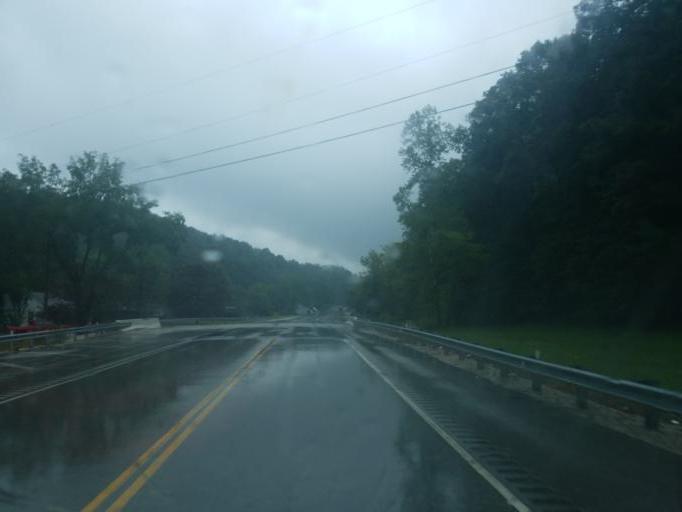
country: US
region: Kentucky
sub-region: Rowan County
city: Morehead
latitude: 38.2476
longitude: -83.3430
